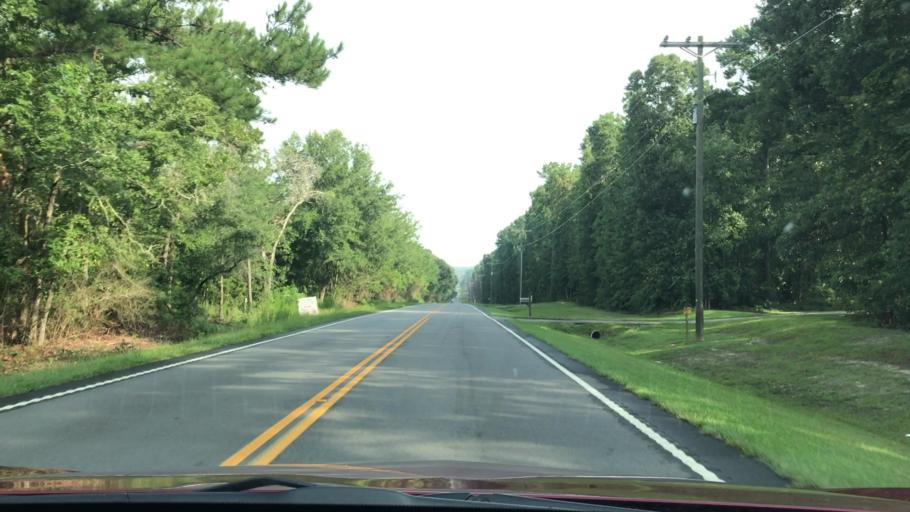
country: US
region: South Carolina
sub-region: Lexington County
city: Batesburg
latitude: 33.7228
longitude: -81.5041
